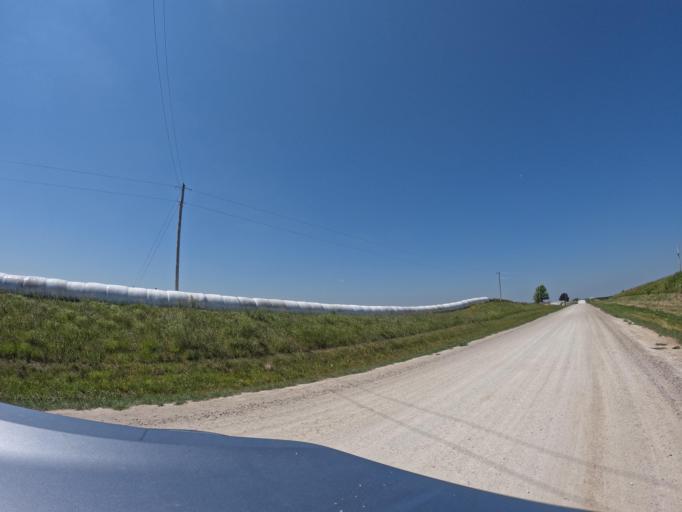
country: US
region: Iowa
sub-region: Keokuk County
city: Sigourney
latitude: 41.2505
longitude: -92.2051
